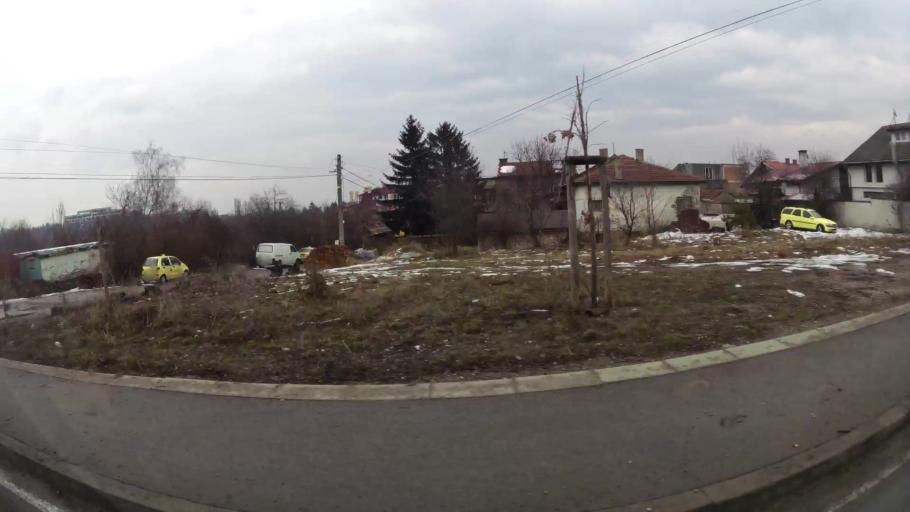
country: BG
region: Sofia-Capital
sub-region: Stolichna Obshtina
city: Sofia
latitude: 42.6698
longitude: 23.2447
